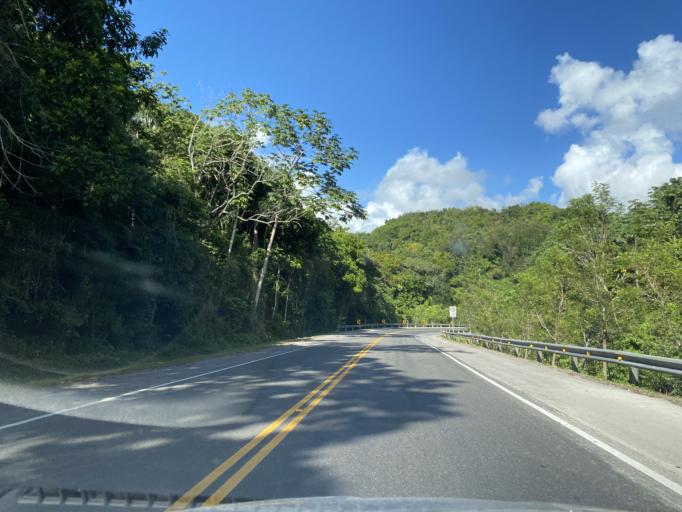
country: DO
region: Monte Plata
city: Majagual
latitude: 19.0576
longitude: -69.8301
